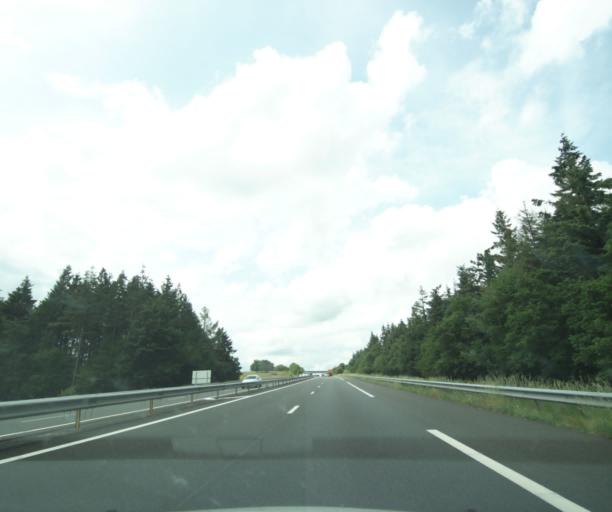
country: FR
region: Auvergne
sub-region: Departement de l'Allier
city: Bellenaves
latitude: 46.2504
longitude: 3.0848
